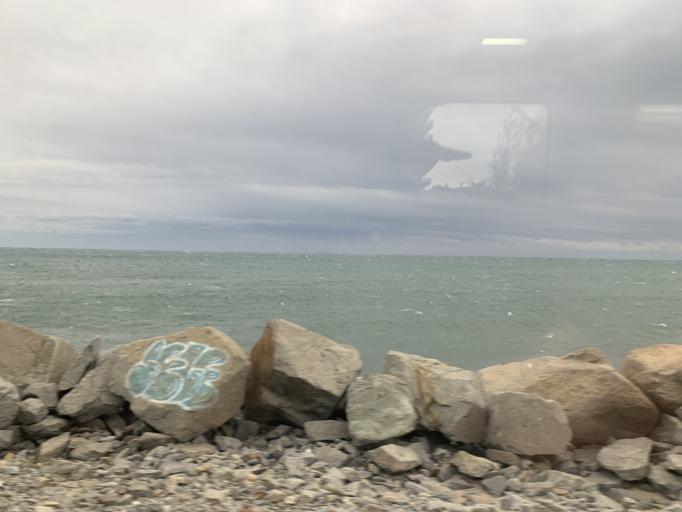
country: ES
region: Catalonia
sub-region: Provincia de Barcelona
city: Mataro
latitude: 41.5254
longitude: 2.4340
